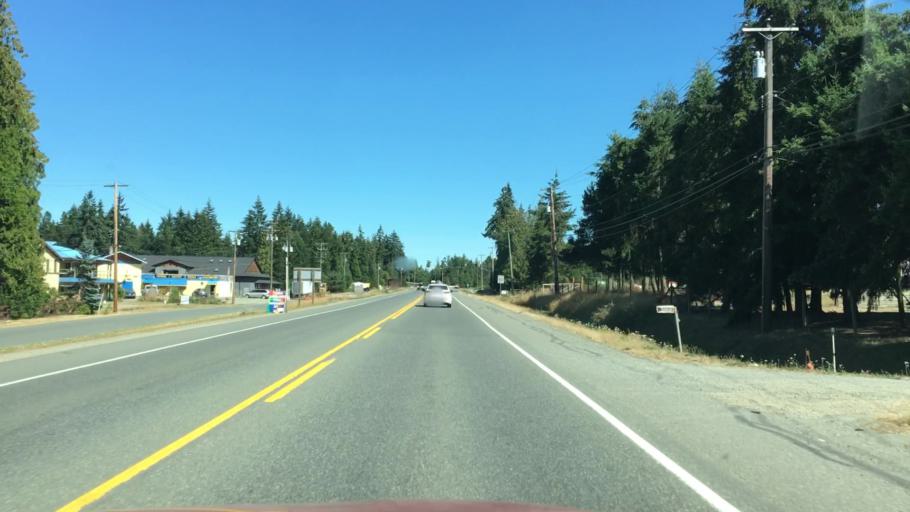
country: CA
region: British Columbia
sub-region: Regional District of Nanaimo
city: Parksville
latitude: 49.3064
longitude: -124.4768
